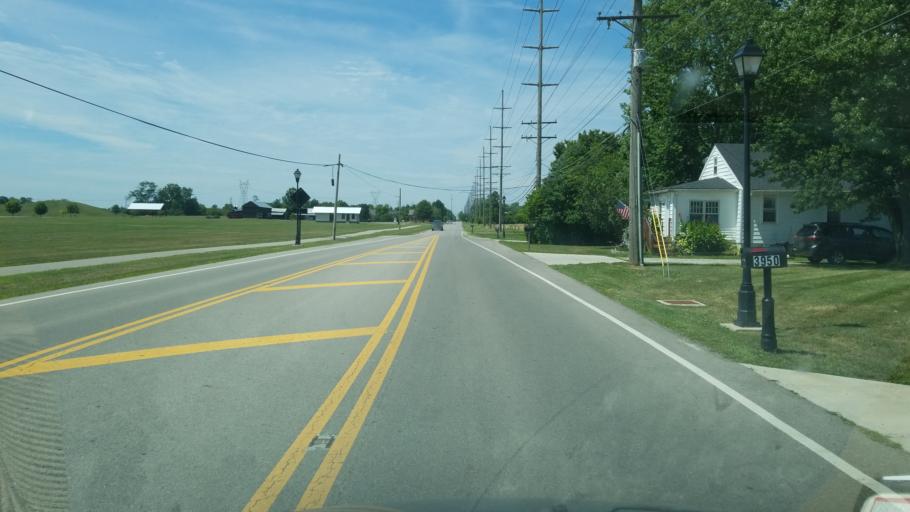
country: US
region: Ohio
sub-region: Franklin County
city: Grove City
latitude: 39.8602
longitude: -83.0991
